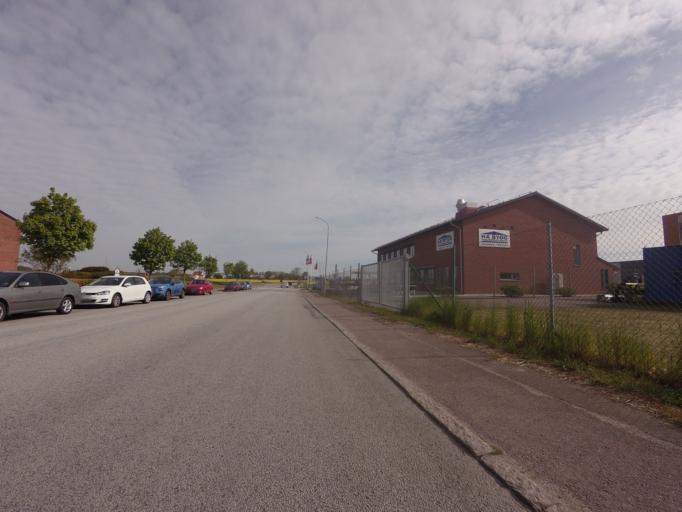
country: SE
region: Skane
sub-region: Hoganas Kommun
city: Hoganas
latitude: 56.2020
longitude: 12.5762
